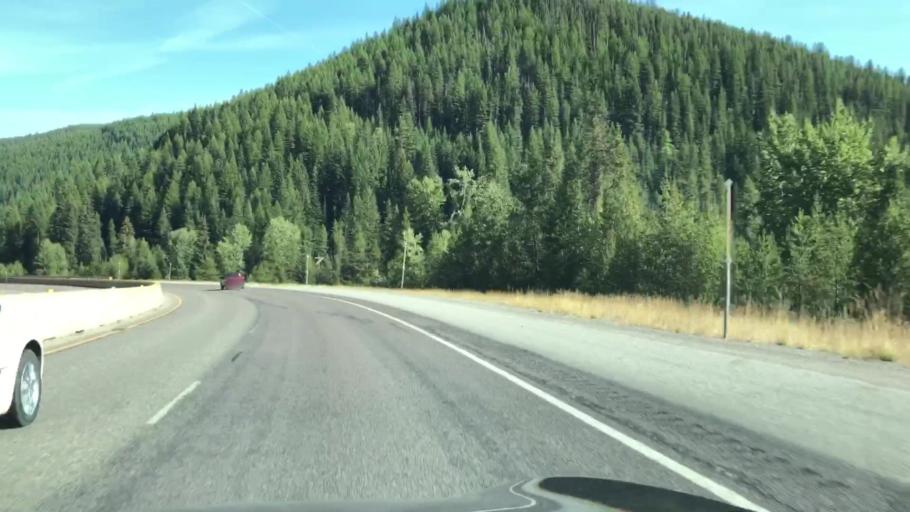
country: US
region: Montana
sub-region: Sanders County
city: Thompson Falls
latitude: 47.4162
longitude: -115.5881
